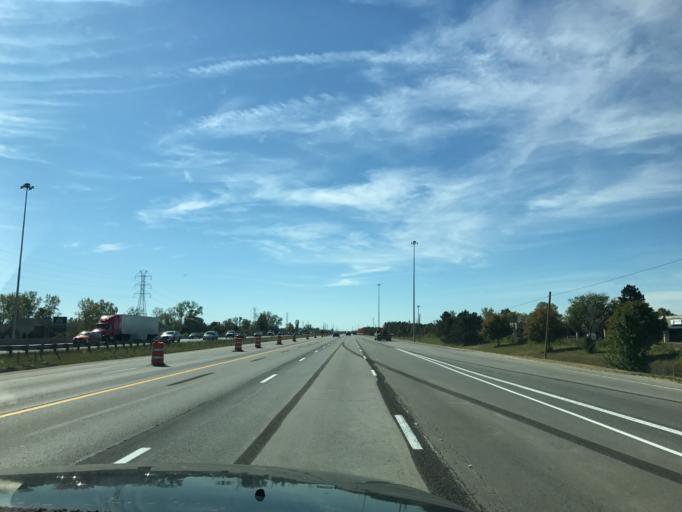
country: US
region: Ohio
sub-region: Franklin County
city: Lincoln Village
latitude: 39.9996
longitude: -83.1185
